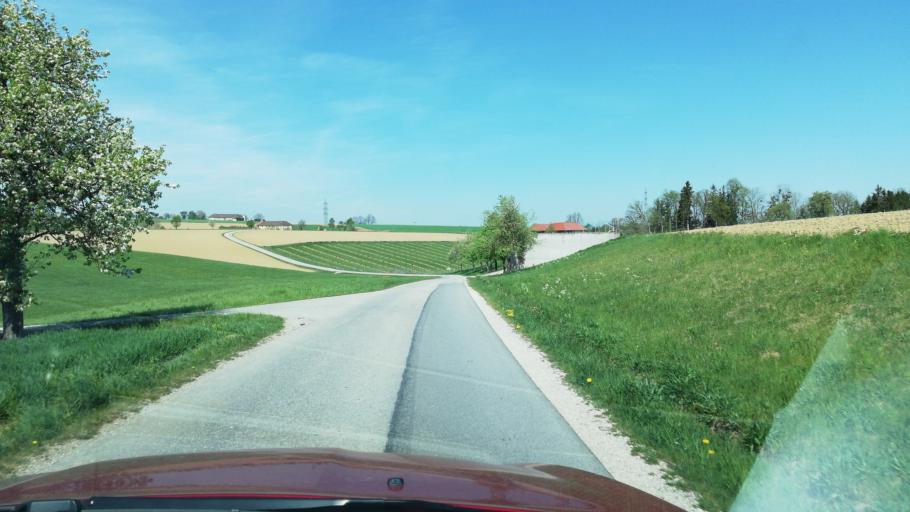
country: AT
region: Upper Austria
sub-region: Politischer Bezirk Steyr-Land
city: Pfarrkirchen bei Bad Hall
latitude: 48.0374
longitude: 14.1774
